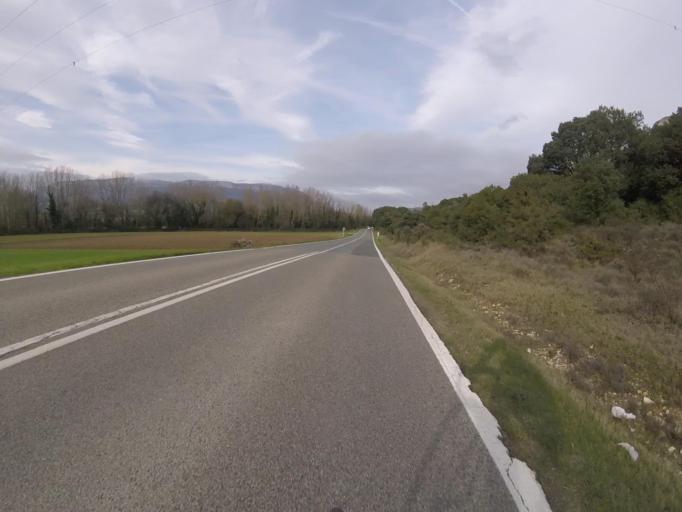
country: ES
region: Navarre
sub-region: Provincia de Navarra
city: Estella
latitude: 42.7045
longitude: -2.0671
